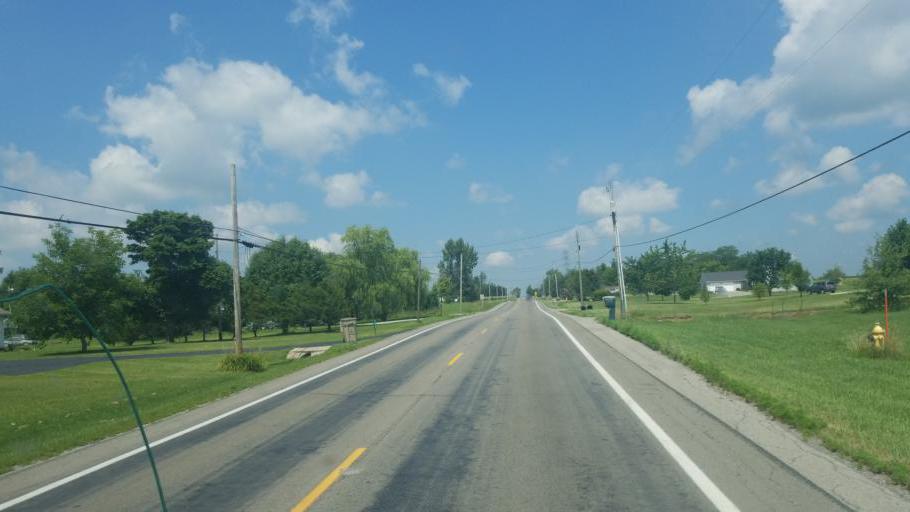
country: US
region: Ohio
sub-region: Allen County
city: Lima
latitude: 40.6985
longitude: -83.9878
